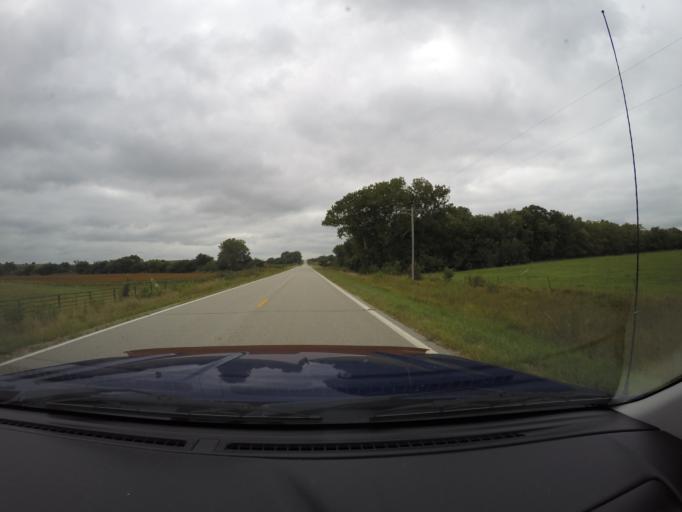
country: US
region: Kansas
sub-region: Morris County
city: Council Grove
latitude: 38.7977
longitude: -96.6258
